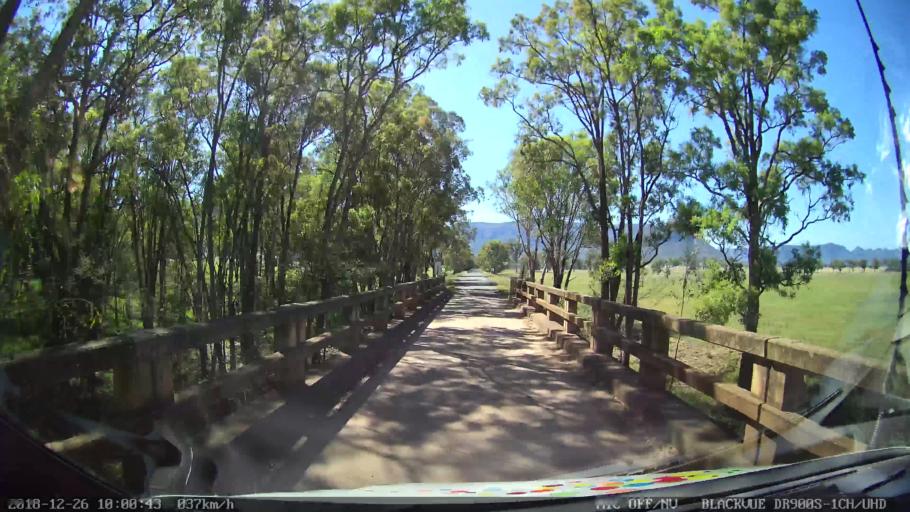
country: AU
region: New South Wales
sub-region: Mid-Western Regional
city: Kandos
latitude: -33.0445
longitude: 150.2175
